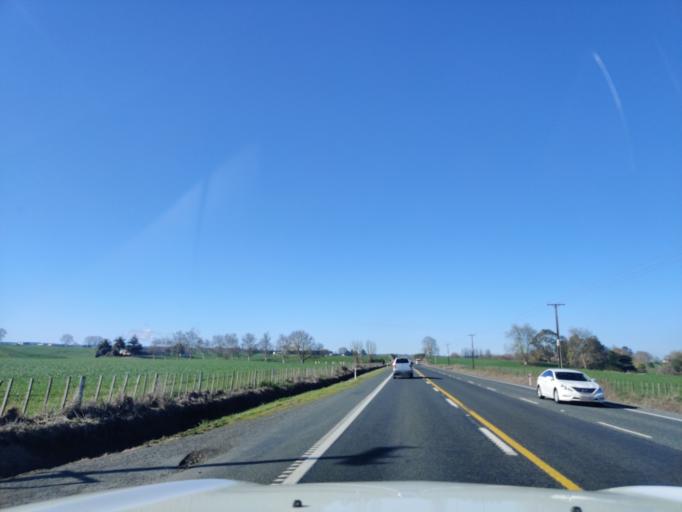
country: NZ
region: Waikato
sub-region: Matamata-Piako District
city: Matamata
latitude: -38.0200
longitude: 175.7825
